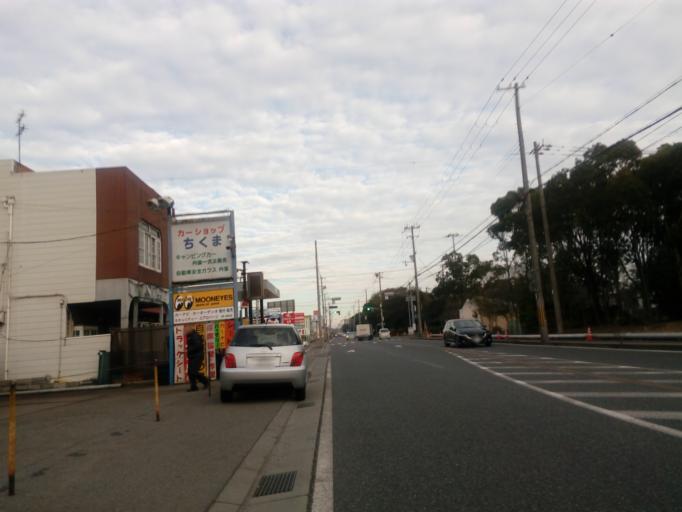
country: JP
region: Hyogo
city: Himeji
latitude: 34.7953
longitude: 134.6219
